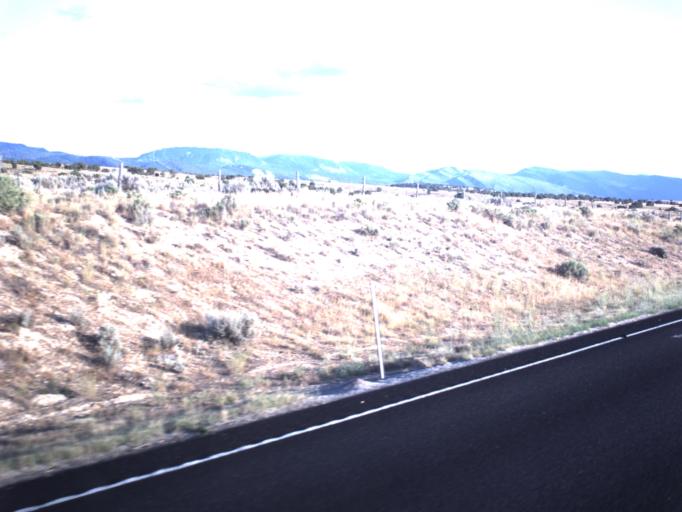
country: US
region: Utah
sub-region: Sanpete County
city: Ephraim
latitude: 39.4365
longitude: -111.5512
